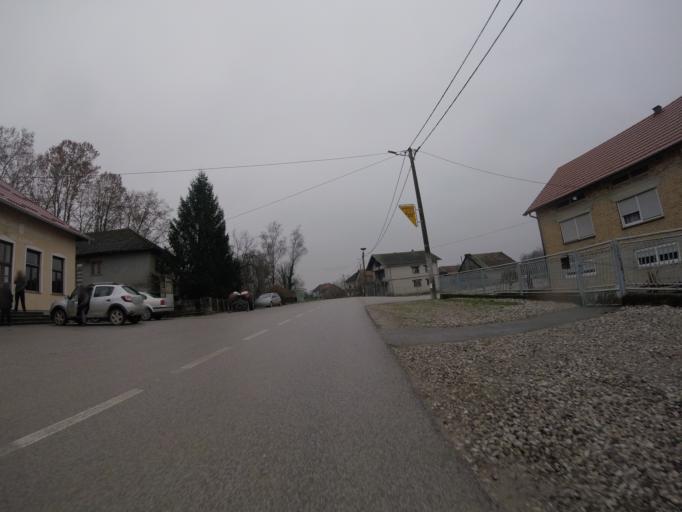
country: HR
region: Sisacko-Moslavacka
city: Lekenik
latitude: 45.6190
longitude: 16.3293
